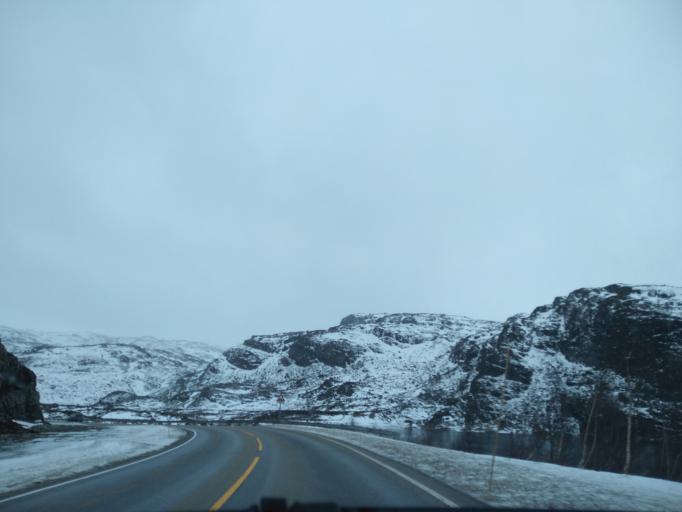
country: NO
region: Vest-Agder
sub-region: Sirdal
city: Tonstad
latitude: 58.9136
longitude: 6.7455
